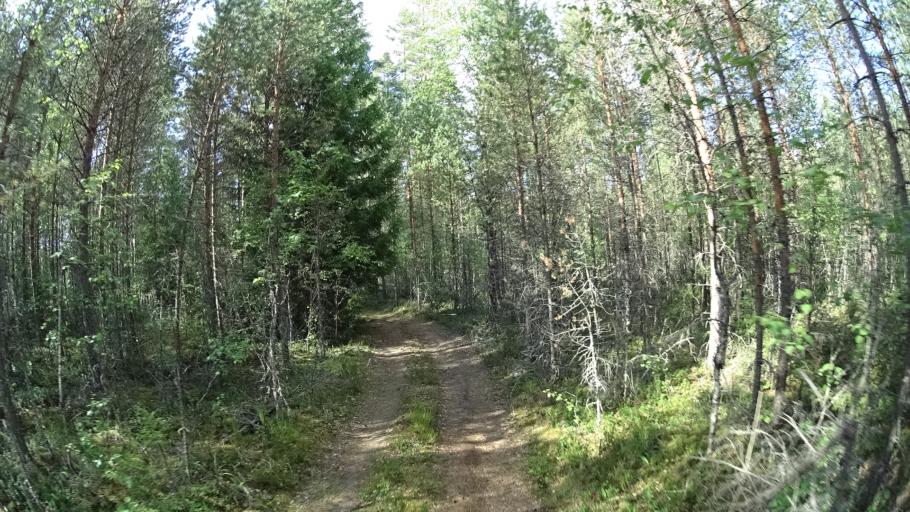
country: FI
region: Uusimaa
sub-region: Helsinki
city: Kaerkoelae
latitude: 60.7338
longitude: 24.0582
